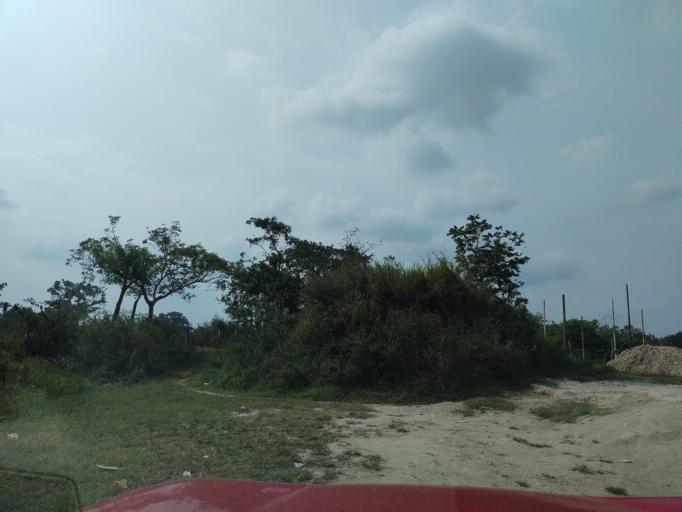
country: MX
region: Veracruz
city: Agua Dulce
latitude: 20.3618
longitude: -97.2985
